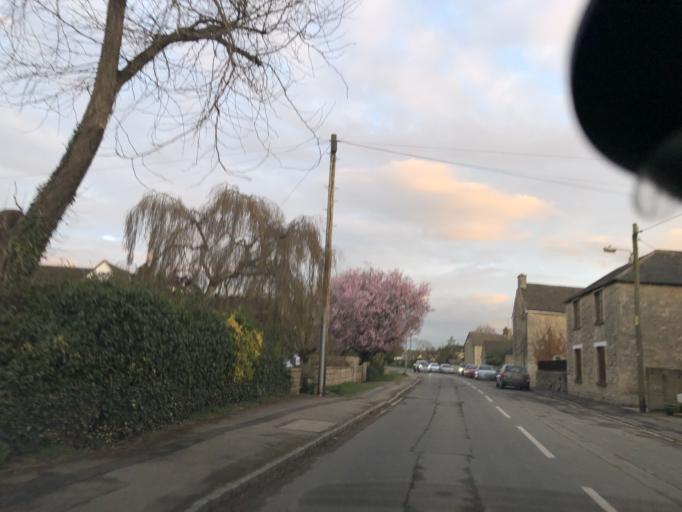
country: GB
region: England
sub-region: Oxfordshire
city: Ducklington
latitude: 51.7712
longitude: -1.4897
